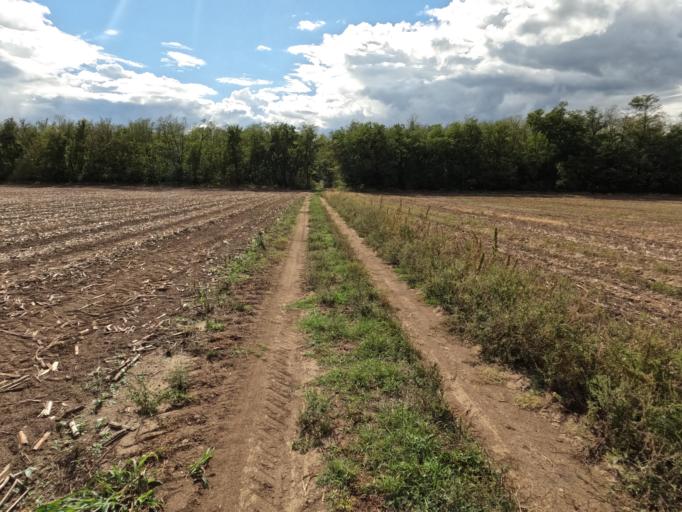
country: HU
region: Tolna
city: Tengelic
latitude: 46.5194
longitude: 18.6791
